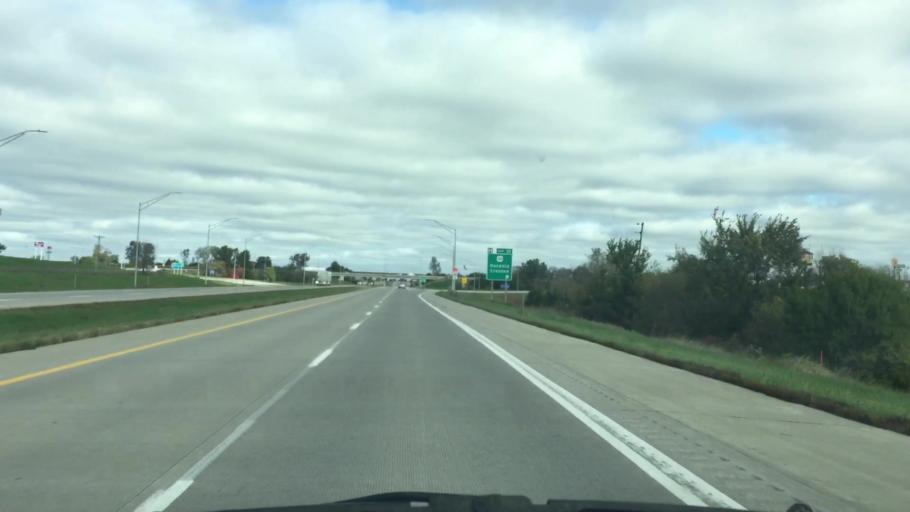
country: US
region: Iowa
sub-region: Clarke County
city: Osceola
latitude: 41.0211
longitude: -93.7939
